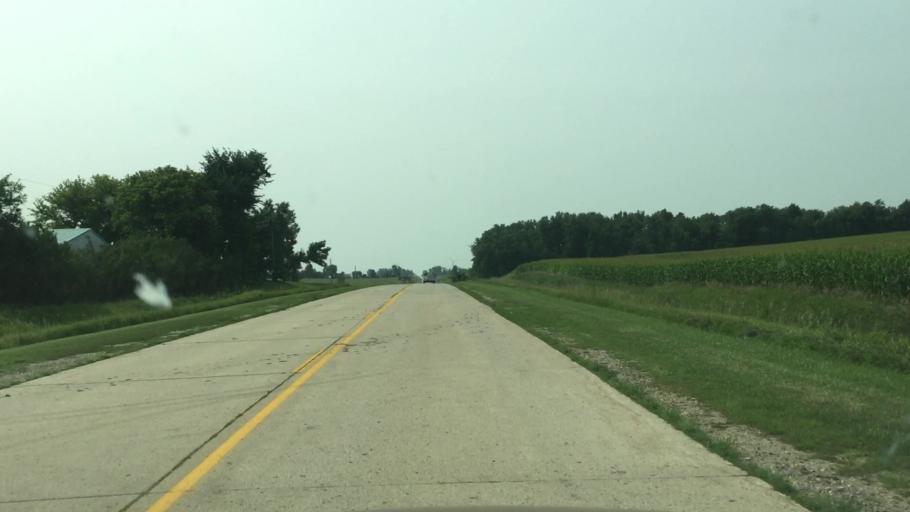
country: US
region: Iowa
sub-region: Dickinson County
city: Lake Park
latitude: 43.4219
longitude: -95.2891
